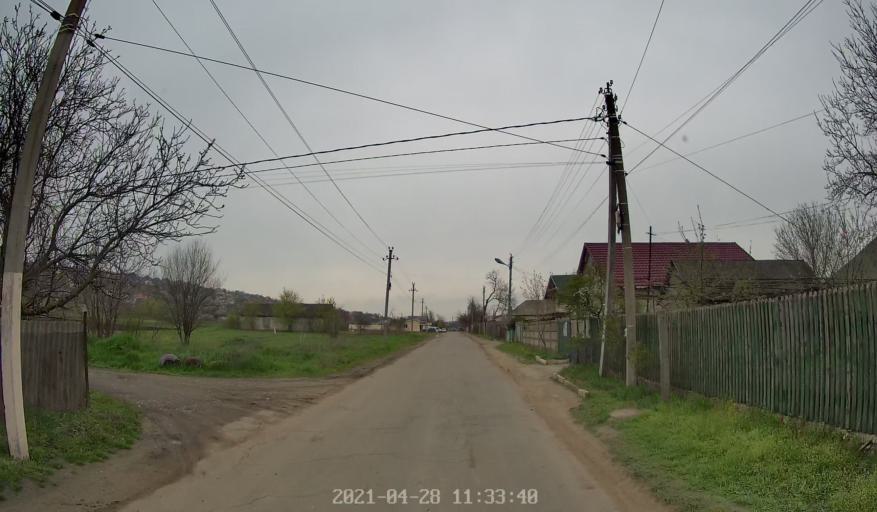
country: MD
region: Chisinau
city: Singera
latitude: 46.9601
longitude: 28.9390
